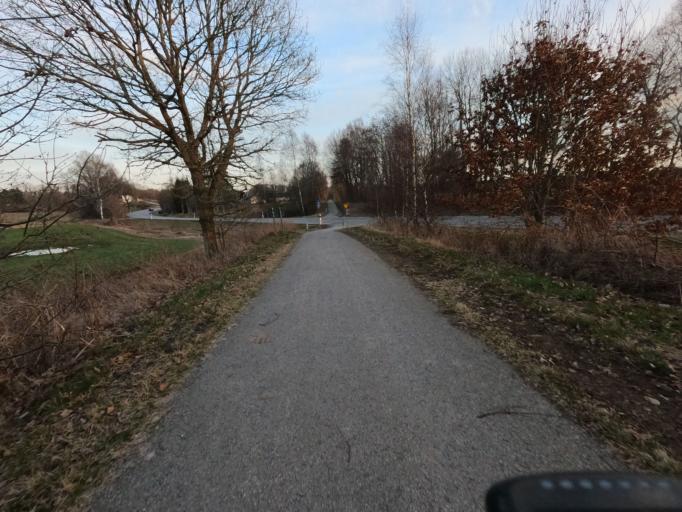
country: SE
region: Blekinge
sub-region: Karlshamns Kommun
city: Svangsta
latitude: 56.2299
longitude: 14.8123
